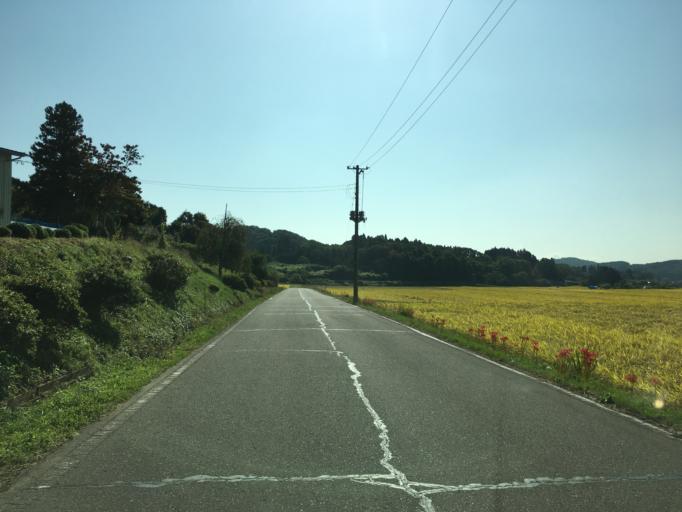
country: JP
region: Fukushima
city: Nihommatsu
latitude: 37.5721
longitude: 140.3921
